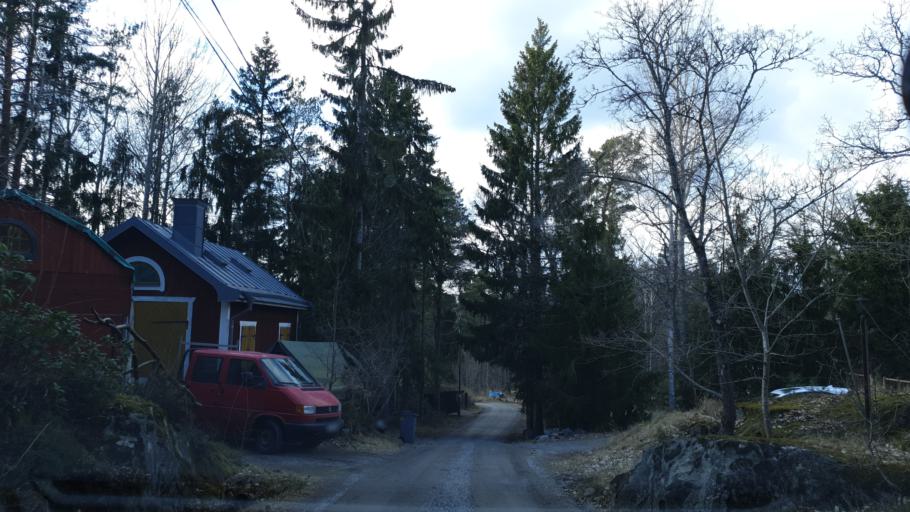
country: SE
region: Stockholm
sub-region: Tyreso Kommun
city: Brevik
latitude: 59.2452
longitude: 18.4446
